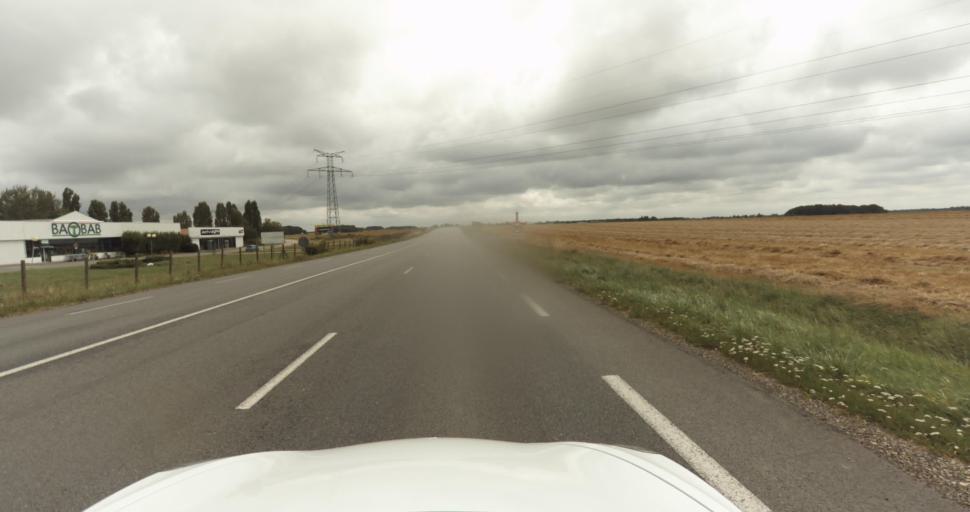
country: FR
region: Haute-Normandie
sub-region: Departement de l'Eure
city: Saint-Sebastien-de-Morsent
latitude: 49.0420
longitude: 1.0797
